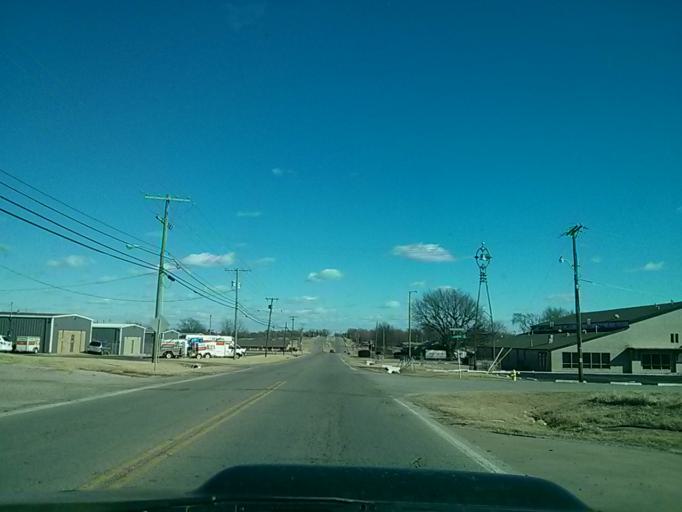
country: US
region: Oklahoma
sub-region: Tulsa County
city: Turley
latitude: 36.2061
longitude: -95.9540
